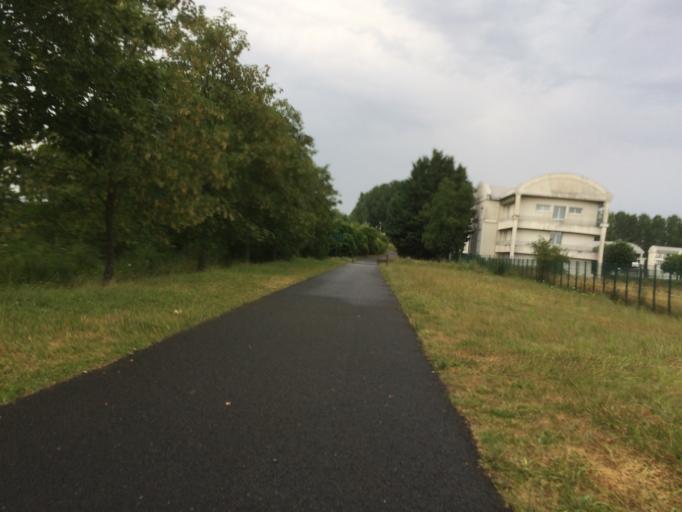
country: FR
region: Picardie
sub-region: Departement de l'Oise
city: Jaux
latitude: 49.3840
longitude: 2.7783
